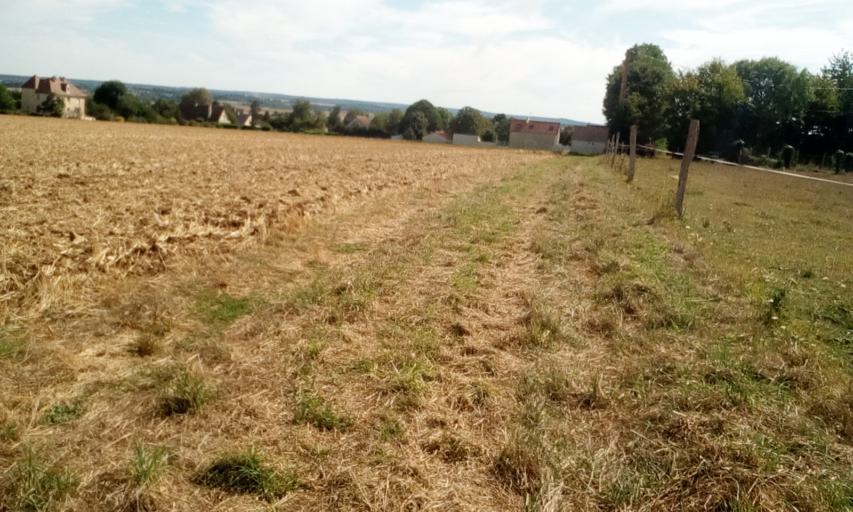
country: FR
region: Lower Normandy
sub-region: Departement du Calvados
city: Bully
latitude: 49.1138
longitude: -0.4322
